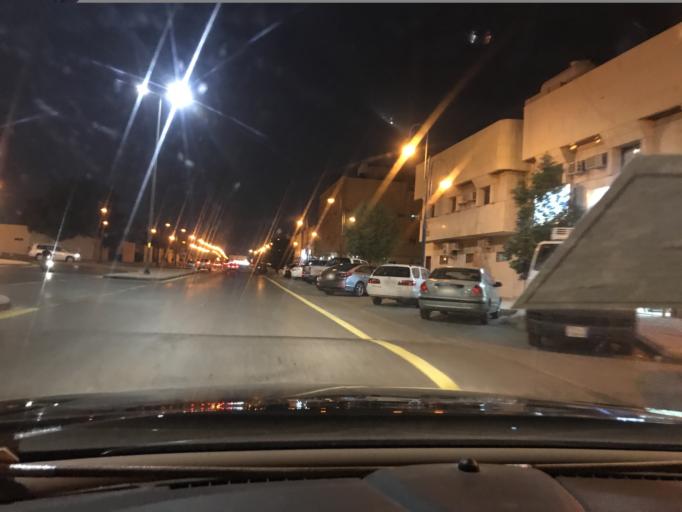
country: SA
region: Ar Riyad
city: Riyadh
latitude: 24.7412
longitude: 46.7701
